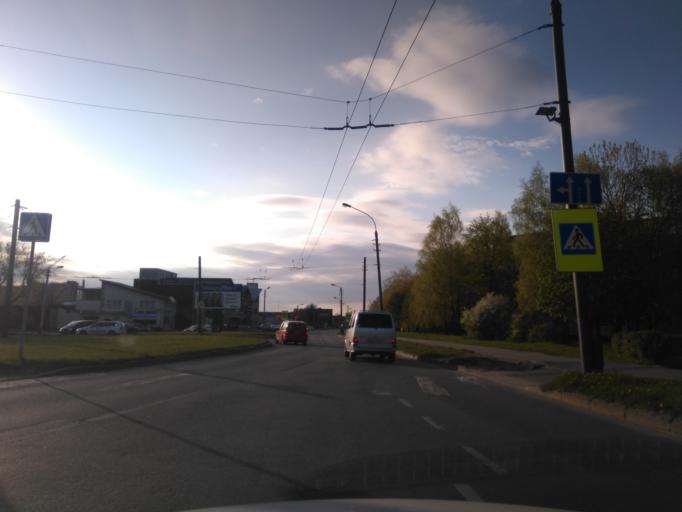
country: LT
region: Kauno apskritis
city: Dainava (Kaunas)
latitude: 54.9150
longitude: 23.9566
